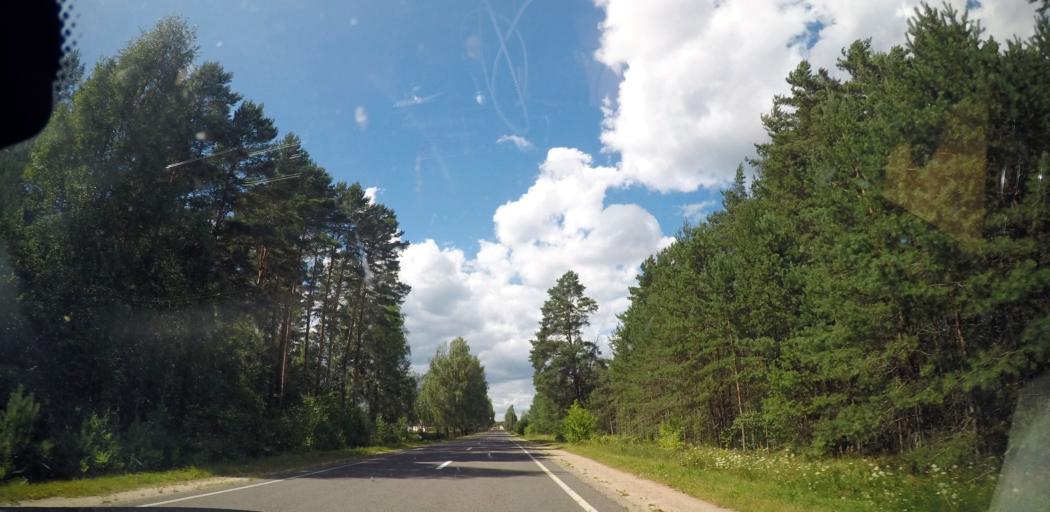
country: LT
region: Alytaus apskritis
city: Druskininkai
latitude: 53.8779
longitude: 24.1454
